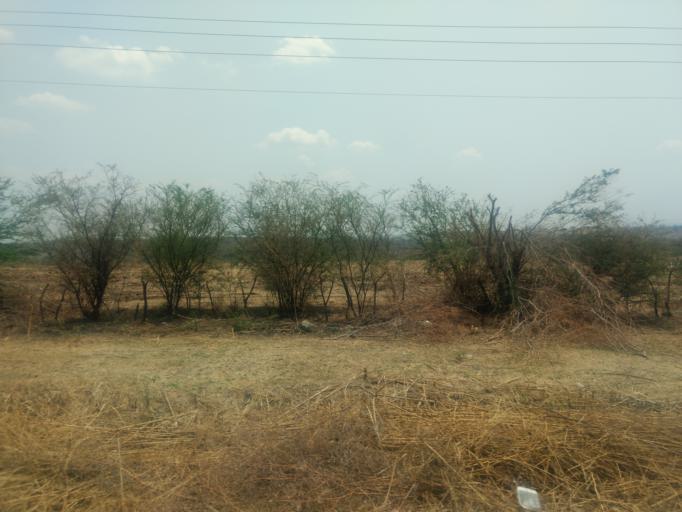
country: MX
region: Morelos
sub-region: Amacuzac
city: Amacuzac
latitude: 18.6249
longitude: -99.3727
